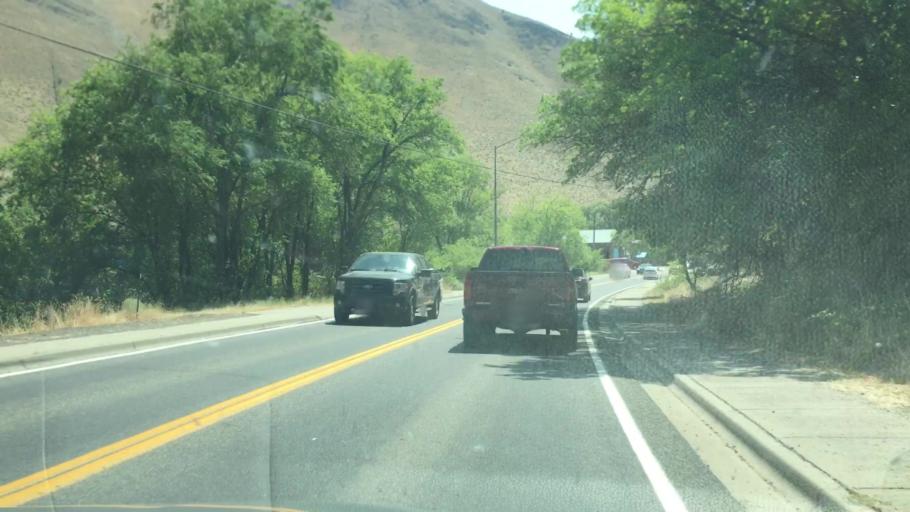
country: US
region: Idaho
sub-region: Idaho County
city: Grangeville
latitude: 45.4285
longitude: -116.3121
